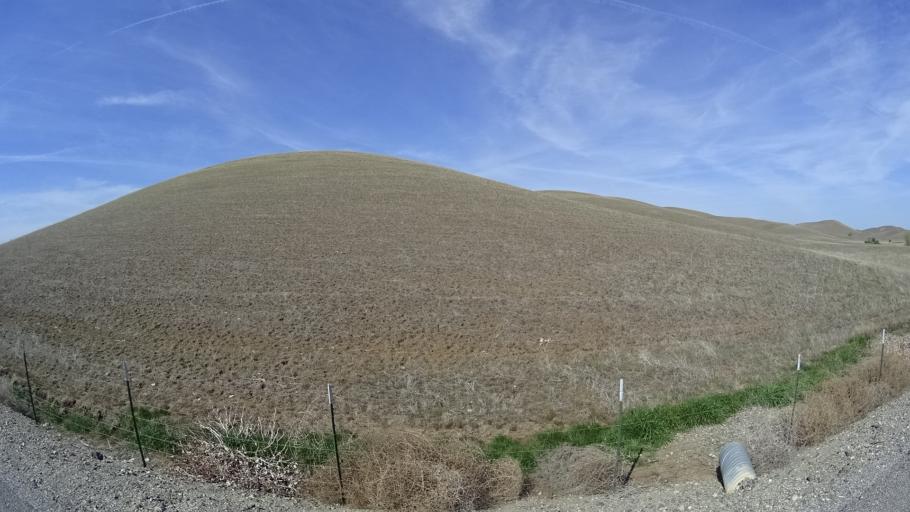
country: US
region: California
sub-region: Glenn County
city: Willows
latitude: 39.5476
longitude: -122.3758
